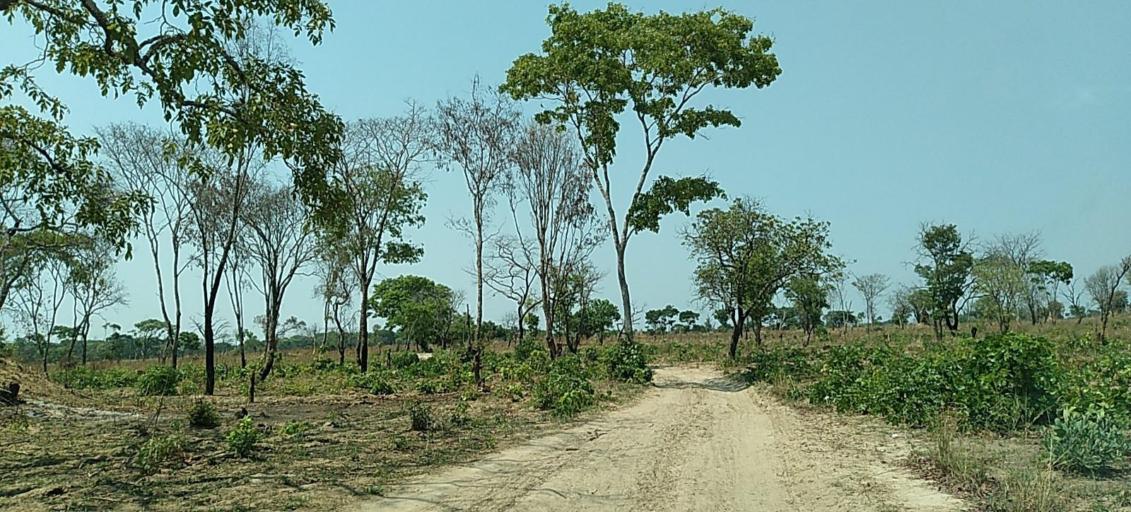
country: ZM
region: Copperbelt
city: Mpongwe
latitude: -13.8586
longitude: 28.0556
